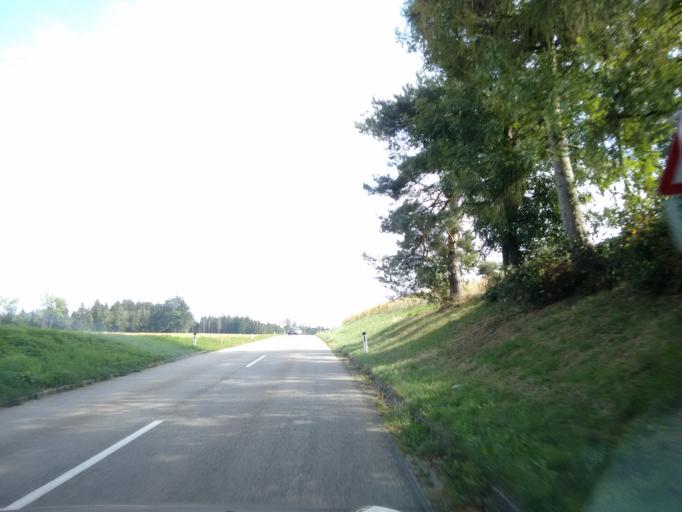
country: AT
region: Upper Austria
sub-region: Wels-Land
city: Thalheim bei Wels
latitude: 48.1391
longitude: 14.0528
